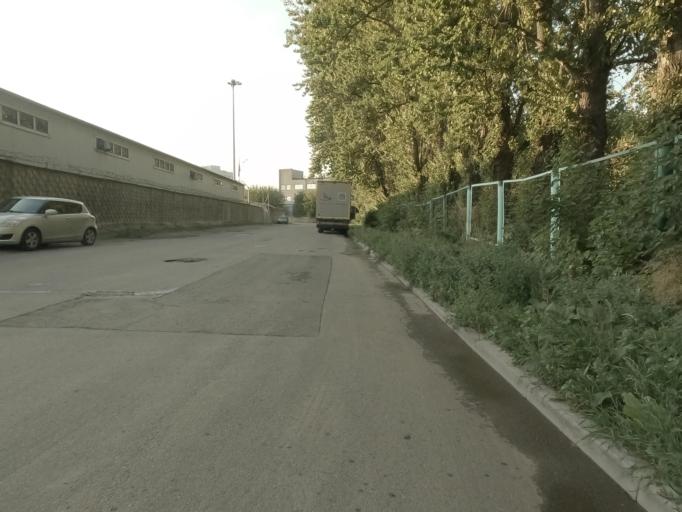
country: RU
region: St.-Petersburg
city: Avtovo
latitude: 59.8948
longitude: 30.2556
